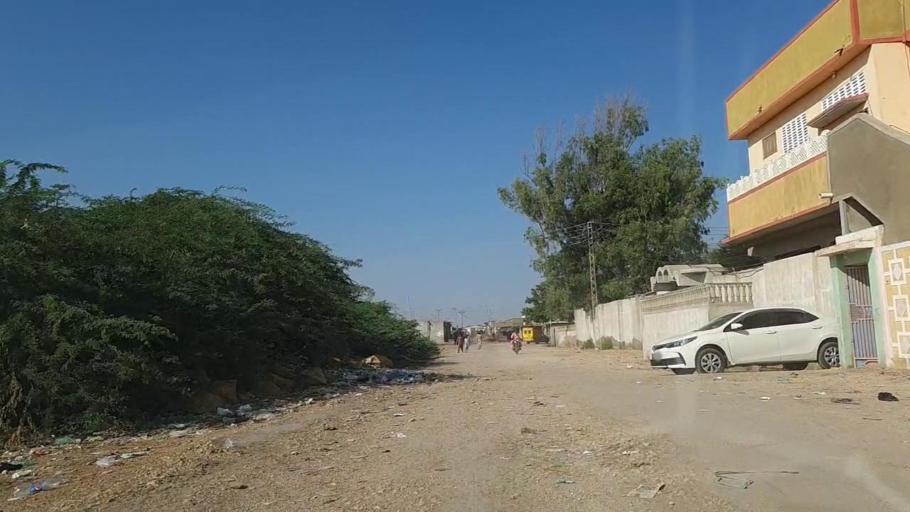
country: PK
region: Sindh
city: Thatta
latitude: 24.6197
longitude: 68.0282
